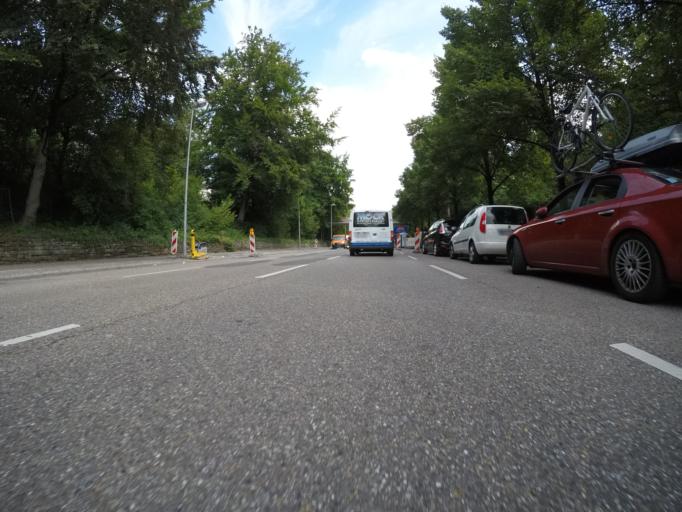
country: DE
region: Baden-Wuerttemberg
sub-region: Regierungsbezirk Stuttgart
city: Stuttgart Feuerbach
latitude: 48.8037
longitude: 9.1743
